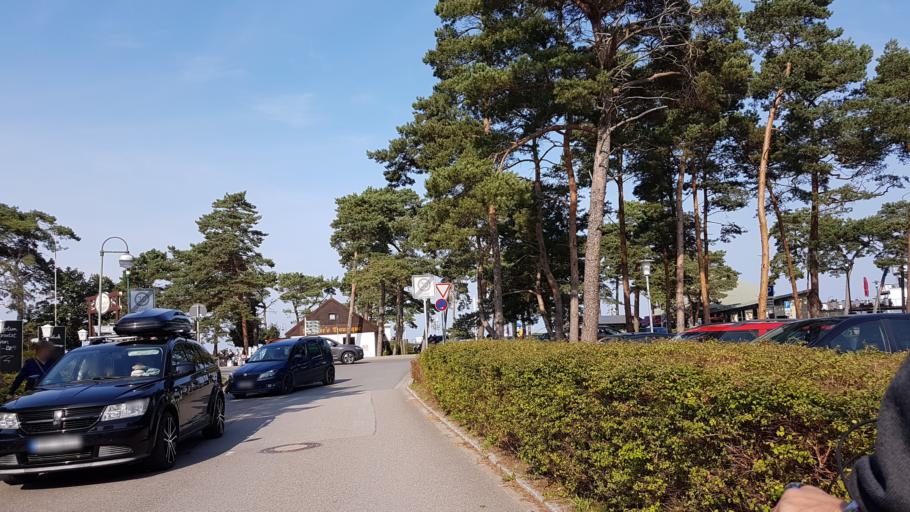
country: DE
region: Mecklenburg-Vorpommern
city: Glowe
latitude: 54.5685
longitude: 13.4588
